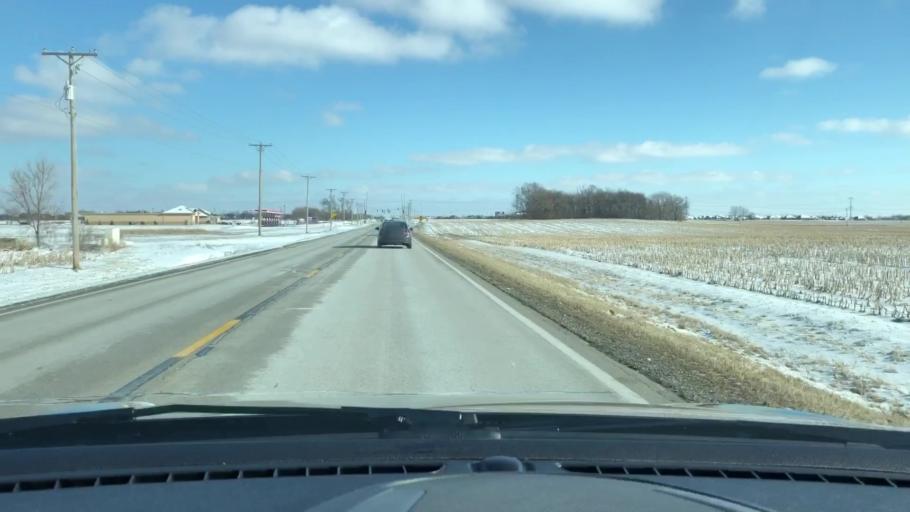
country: US
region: Illinois
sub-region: Will County
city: New Lenox
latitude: 41.4830
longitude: -87.9701
